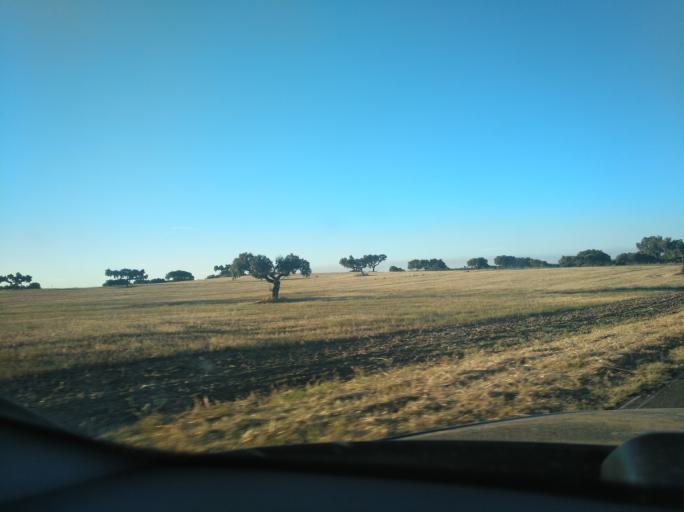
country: PT
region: Portalegre
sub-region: Arronches
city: Arronches
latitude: 39.0748
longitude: -7.1769
